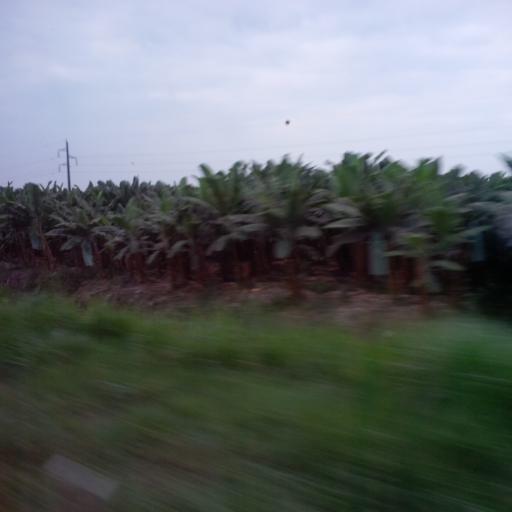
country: EC
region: Canar
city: La Troncal
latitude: -2.3448
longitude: -79.3692
